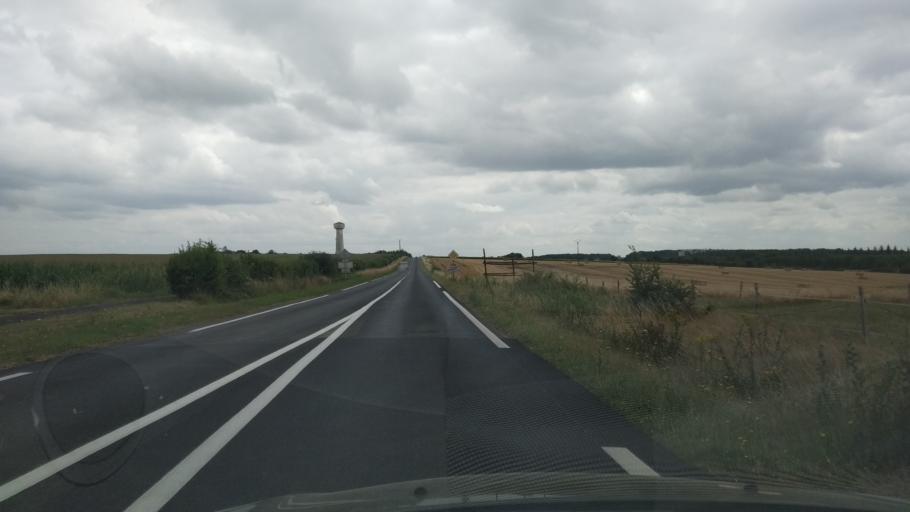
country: FR
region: Poitou-Charentes
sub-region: Departement de la Vienne
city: Roches-Premarie-Andille
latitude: 46.4762
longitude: 0.3691
